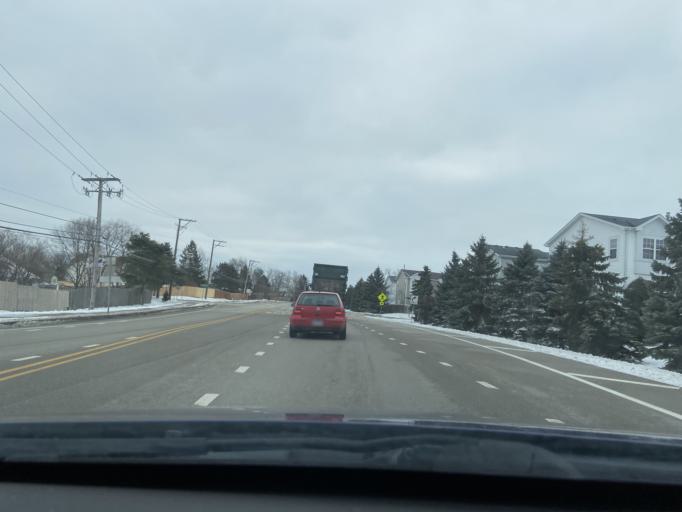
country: US
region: Illinois
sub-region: Lake County
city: Round Lake Park
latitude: 42.3560
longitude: -88.0678
